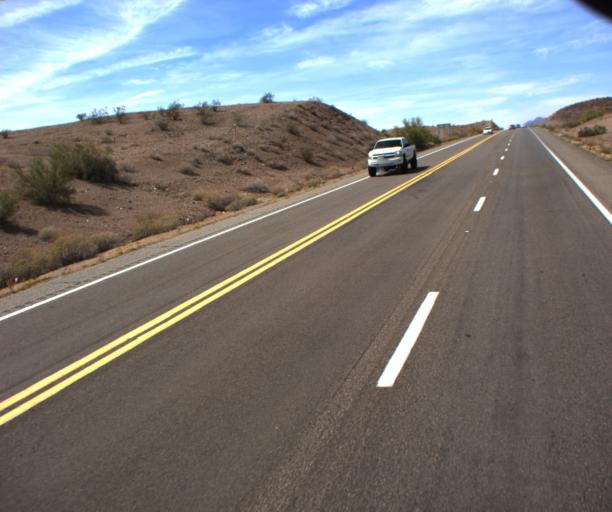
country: US
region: Arizona
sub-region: La Paz County
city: Cienega Springs
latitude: 34.3730
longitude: -114.1624
